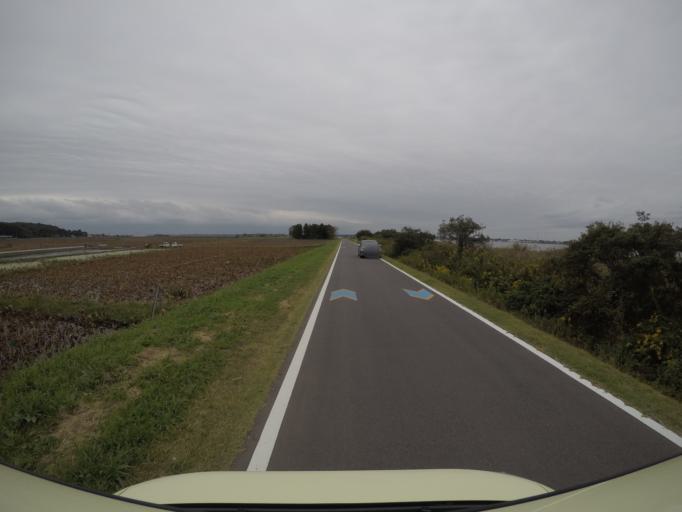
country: JP
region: Ibaraki
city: Ami
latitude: 36.0780
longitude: 140.2393
